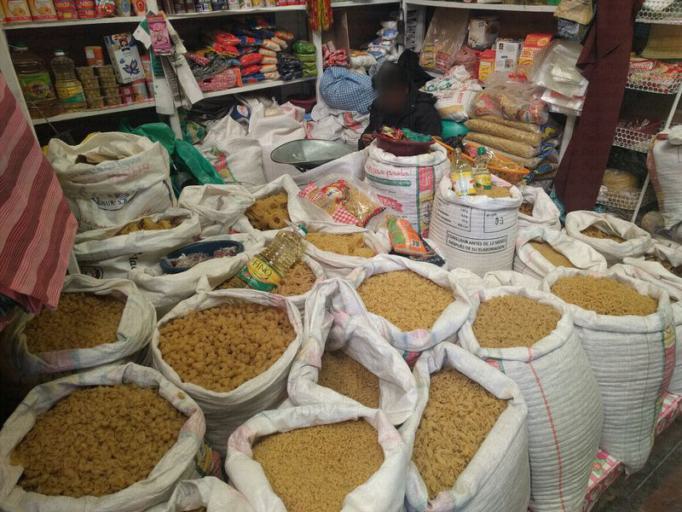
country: BO
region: Potosi
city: Uyuni
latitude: -20.4641
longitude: -66.8268
